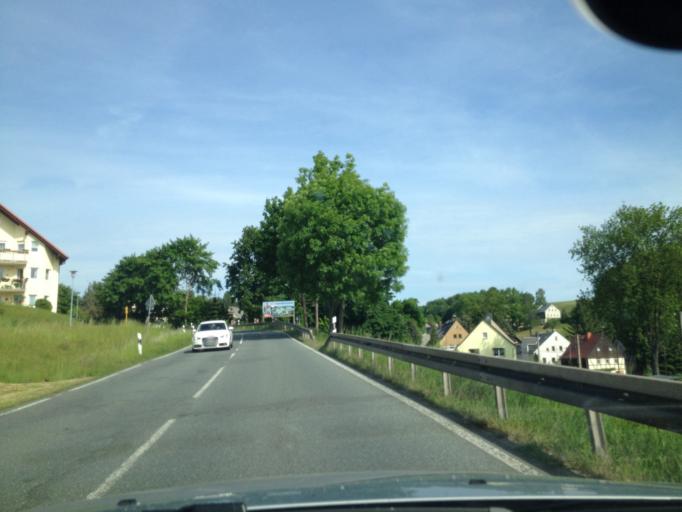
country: DE
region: Saxony
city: Wiesa
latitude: 50.6124
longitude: 12.9895
